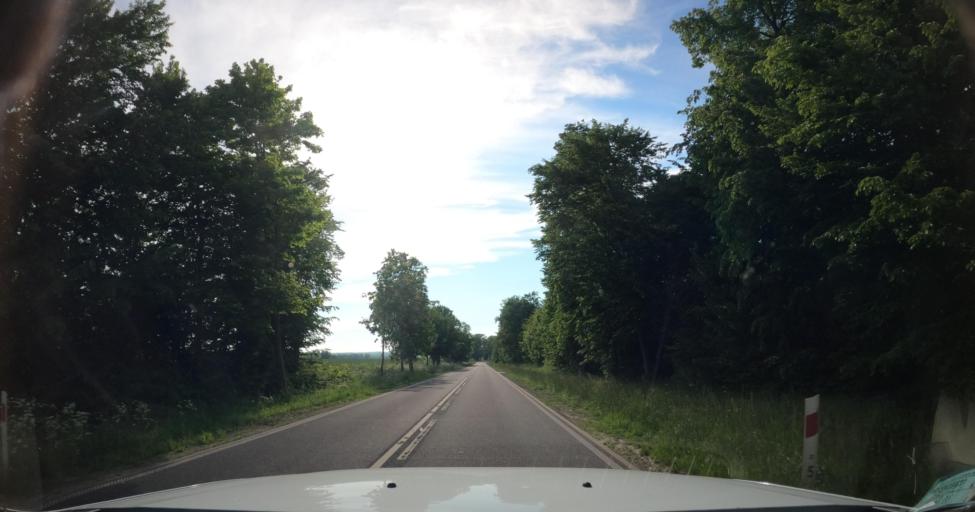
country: PL
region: Warmian-Masurian Voivodeship
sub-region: Powiat ostrodzki
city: Morag
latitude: 54.0823
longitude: 19.8894
